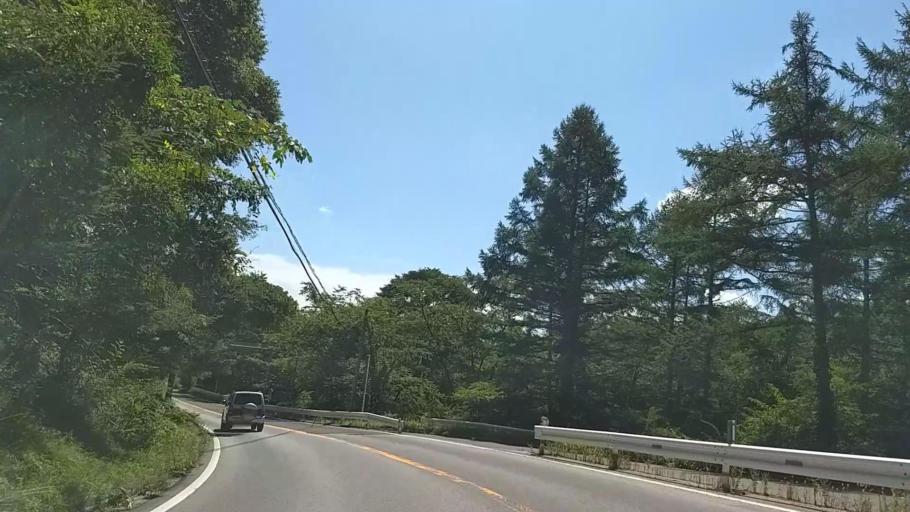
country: JP
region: Nagano
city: Chino
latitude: 36.0794
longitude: 138.2213
